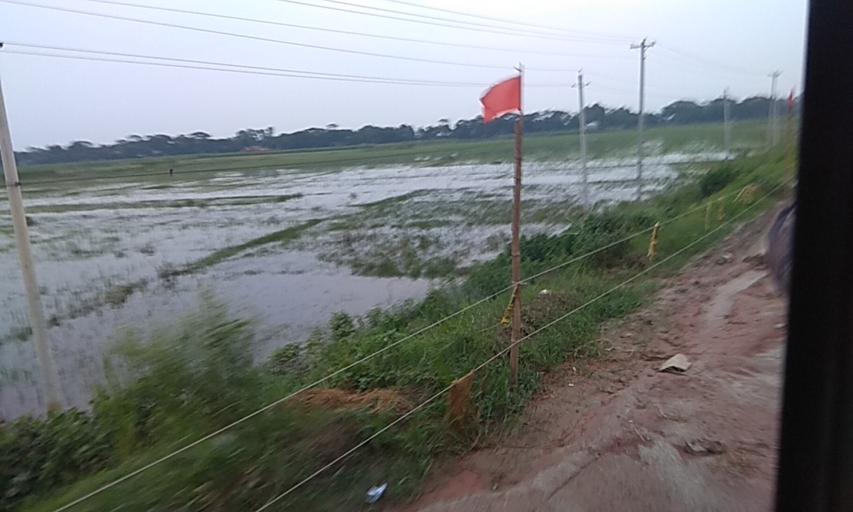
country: BD
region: Dhaka
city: Char Bhadrasan
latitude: 23.3834
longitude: 89.9996
